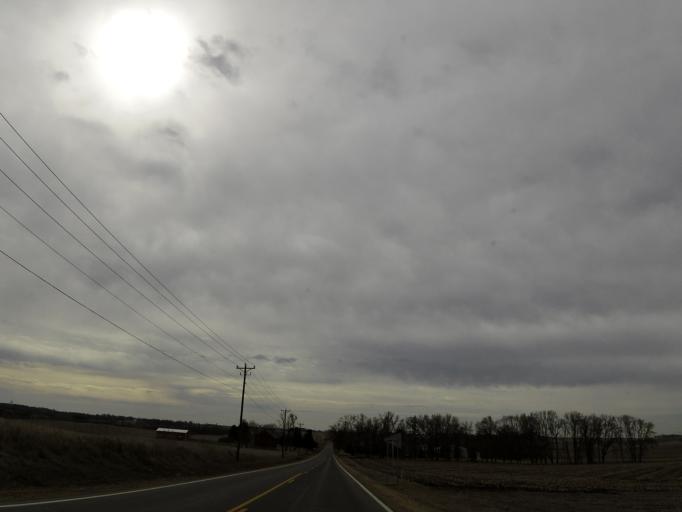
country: US
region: Minnesota
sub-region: Washington County
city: Afton
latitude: 44.8725
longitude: -92.8427
